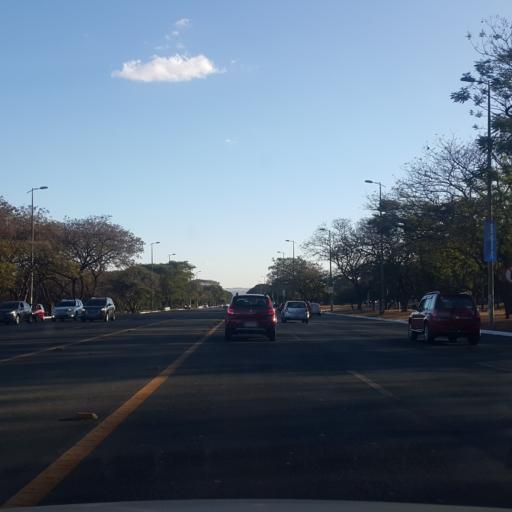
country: BR
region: Federal District
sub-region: Brasilia
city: Brasilia
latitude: -15.8202
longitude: -47.9052
